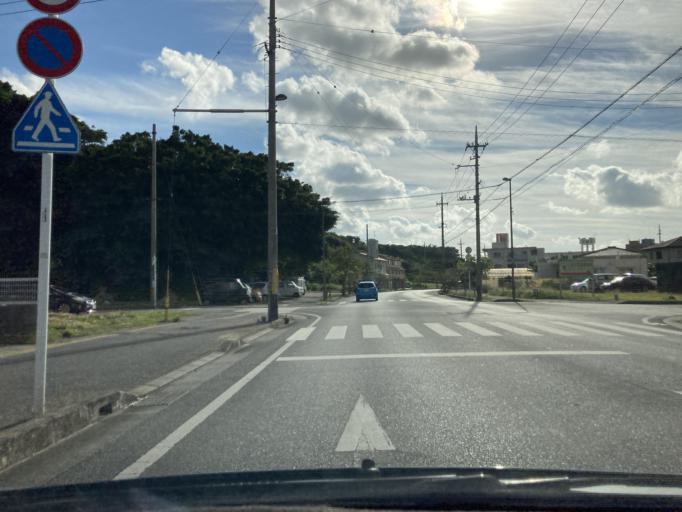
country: JP
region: Okinawa
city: Itoman
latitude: 26.1209
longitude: 127.6725
